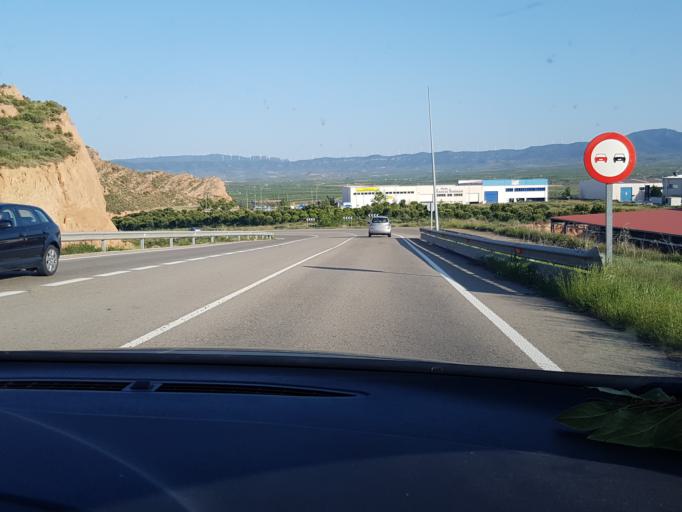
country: ES
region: La Rioja
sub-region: Provincia de La Rioja
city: Arnedo
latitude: 42.2373
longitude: -2.0854
